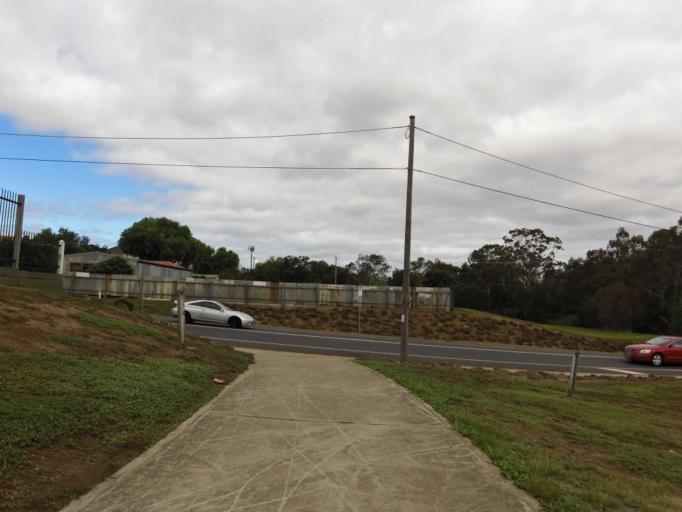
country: AU
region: Victoria
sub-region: Wyndham
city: Werribee
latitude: -37.8987
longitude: 144.6576
